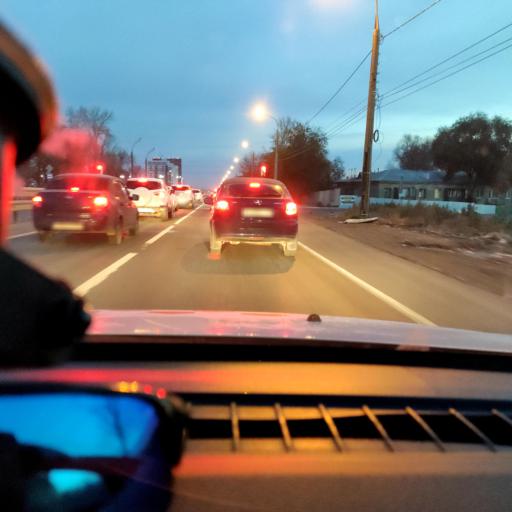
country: RU
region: Samara
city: Samara
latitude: 53.1108
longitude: 50.1651
